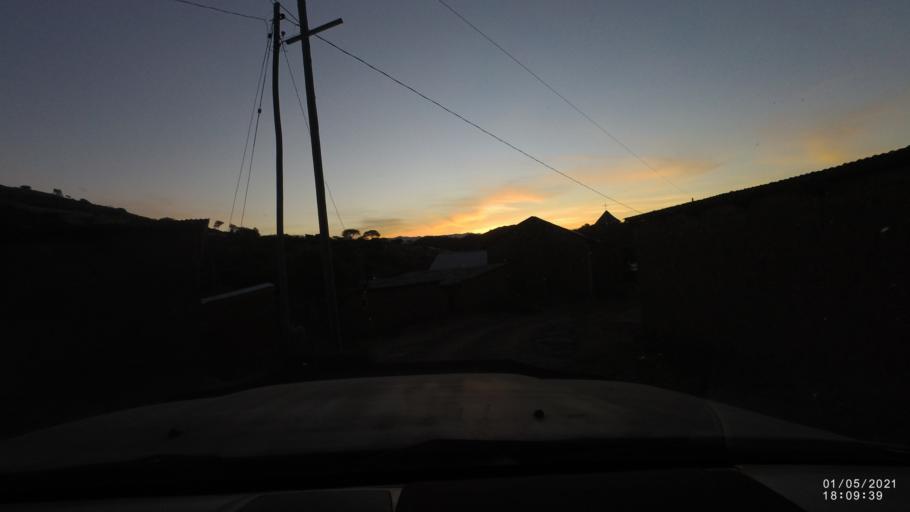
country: BO
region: Cochabamba
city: Capinota
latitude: -17.6861
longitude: -66.1942
